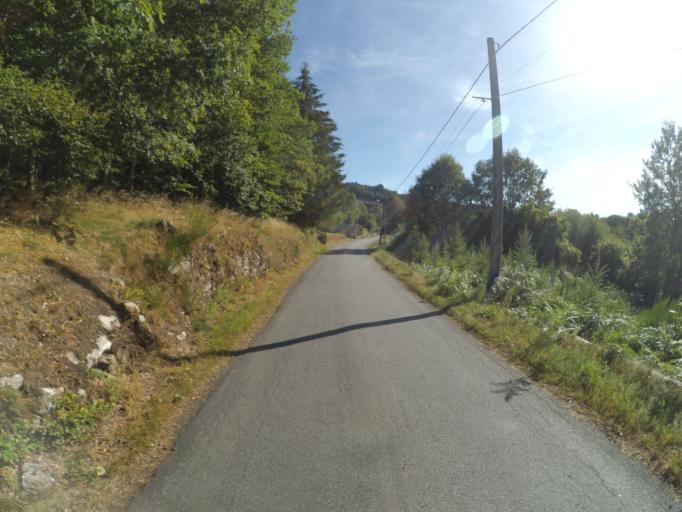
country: FR
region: Limousin
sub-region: Departement de la Correze
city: Bugeat
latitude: 45.6832
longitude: 1.9560
